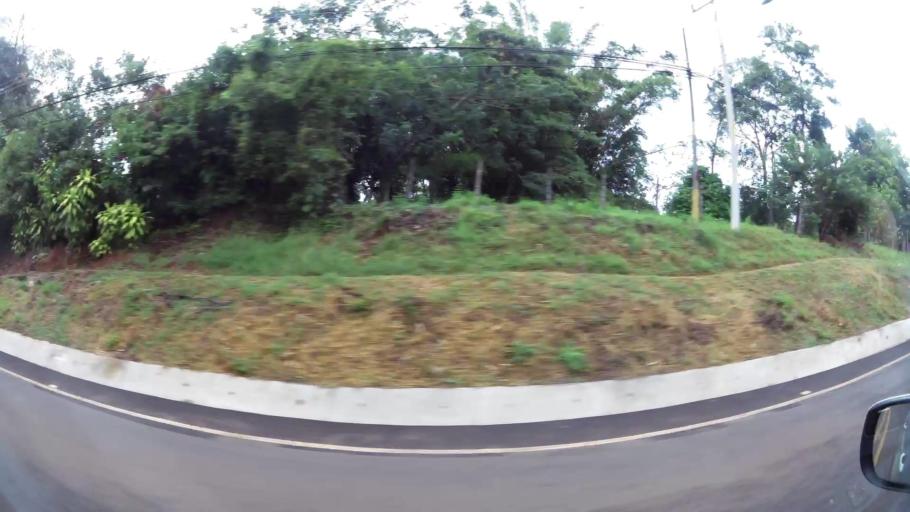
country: CR
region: Puntarenas
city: Esparza
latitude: 9.9595
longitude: -84.5953
